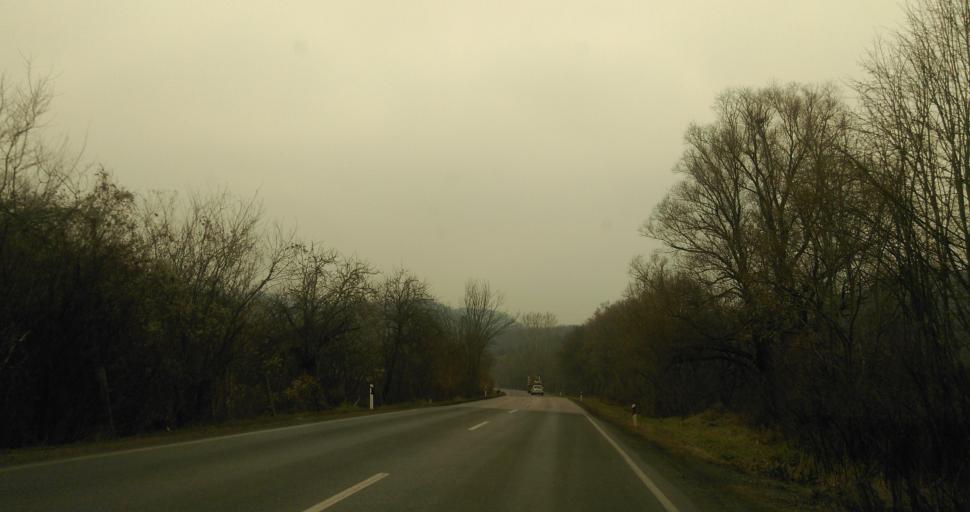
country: RS
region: Central Serbia
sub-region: Belgrade
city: Zvezdara
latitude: 44.7333
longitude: 20.5541
